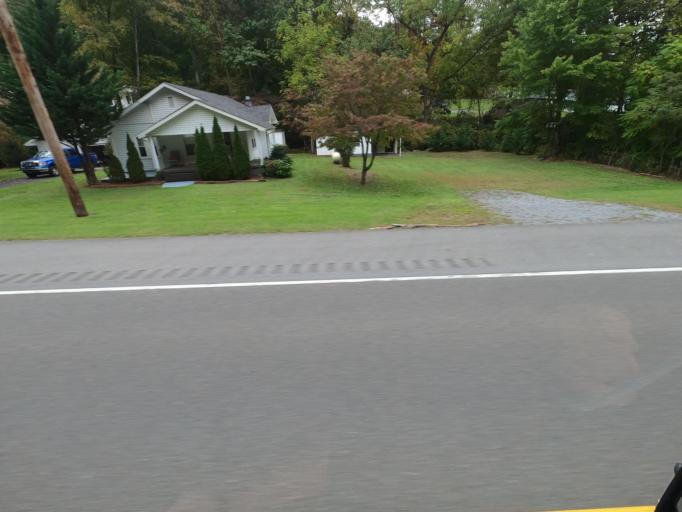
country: US
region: Tennessee
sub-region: Carter County
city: Elizabethton
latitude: 36.2746
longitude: -82.2310
